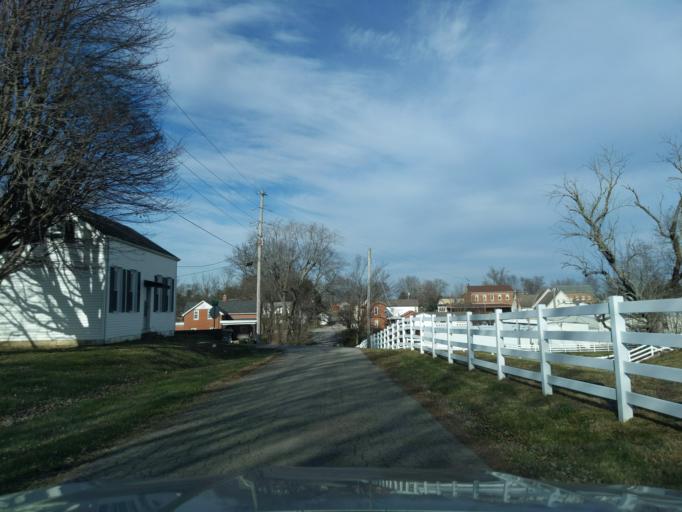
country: US
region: Indiana
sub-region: Decatur County
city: Greensburg
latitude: 39.2088
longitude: -85.4327
